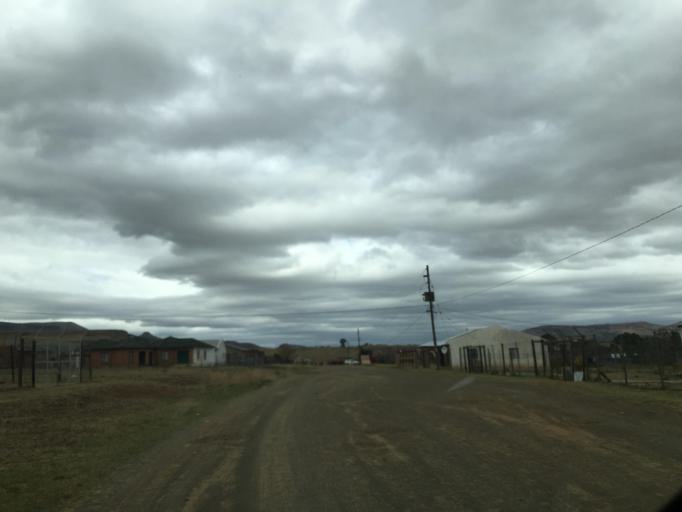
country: ZA
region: Eastern Cape
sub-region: Chris Hani District Municipality
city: Cala
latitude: -31.5360
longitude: 27.6910
